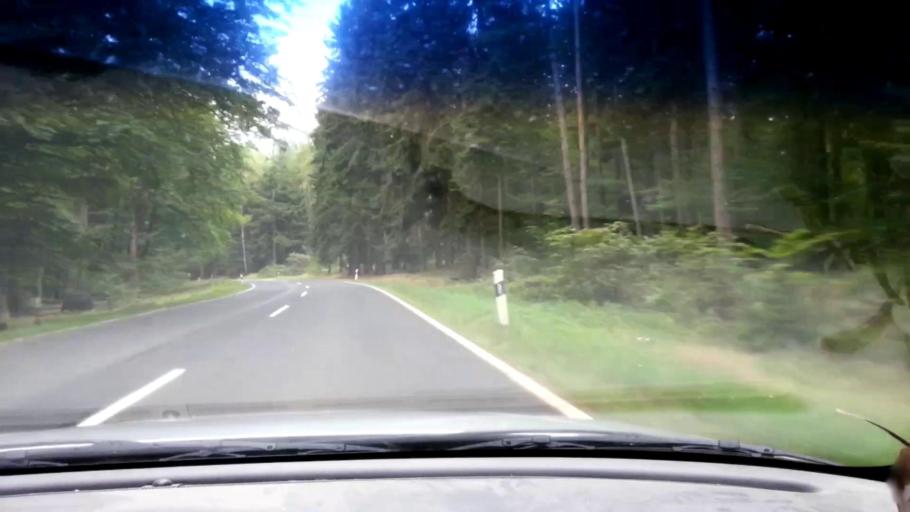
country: DE
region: Bavaria
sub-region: Upper Palatinate
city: Waldsassen
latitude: 50.0241
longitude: 12.3086
